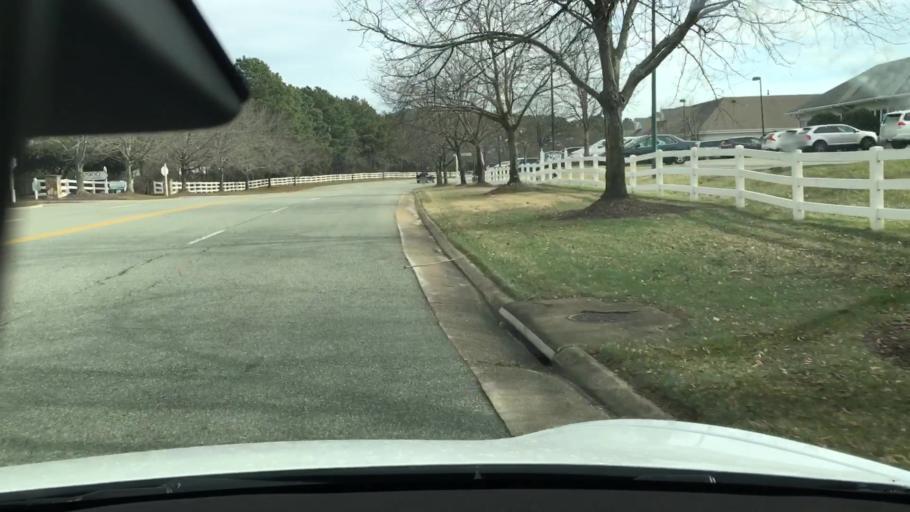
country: US
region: Virginia
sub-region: Chesterfield County
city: Bon Air
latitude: 37.5272
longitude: -77.6107
